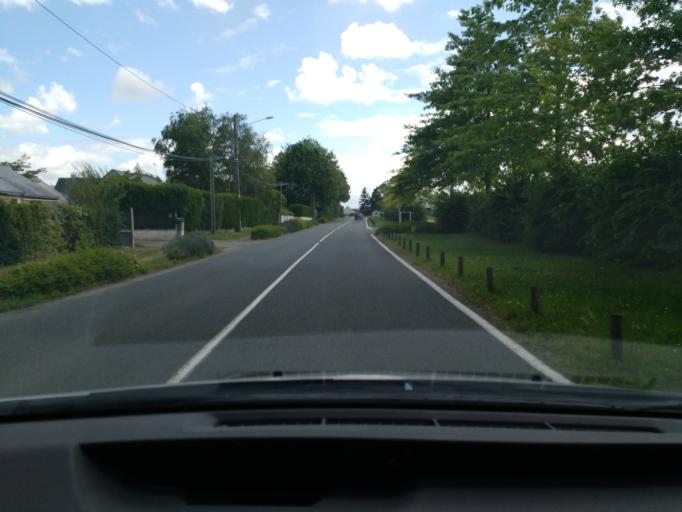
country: FR
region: Pays de la Loire
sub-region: Departement de Maine-et-Loire
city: Le Plessis-Grammoire
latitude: 47.4953
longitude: -0.4338
